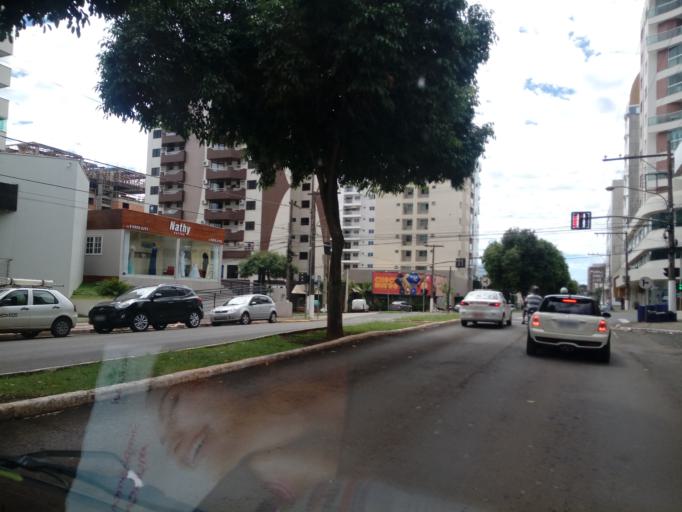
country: BR
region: Santa Catarina
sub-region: Chapeco
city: Chapeco
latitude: -27.0950
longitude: -52.6153
